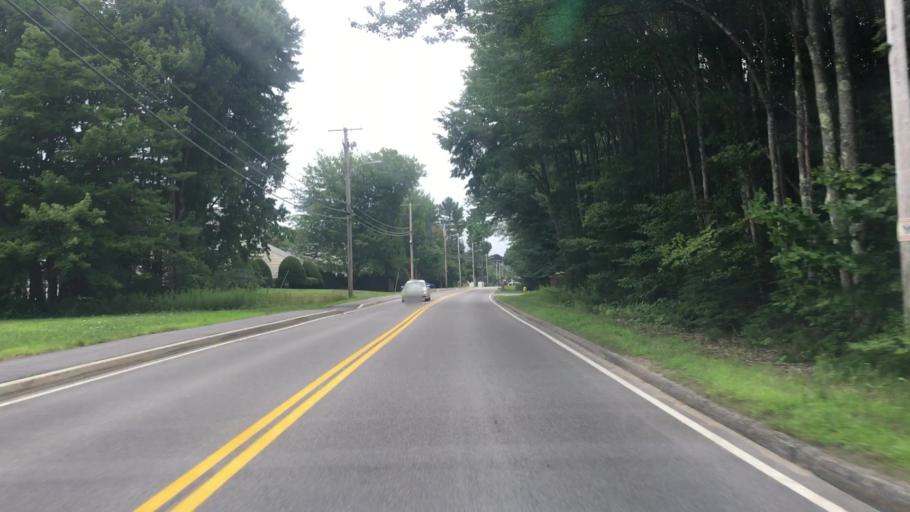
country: US
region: Maine
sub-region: York County
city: Biddeford
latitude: 43.5088
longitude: -70.4602
